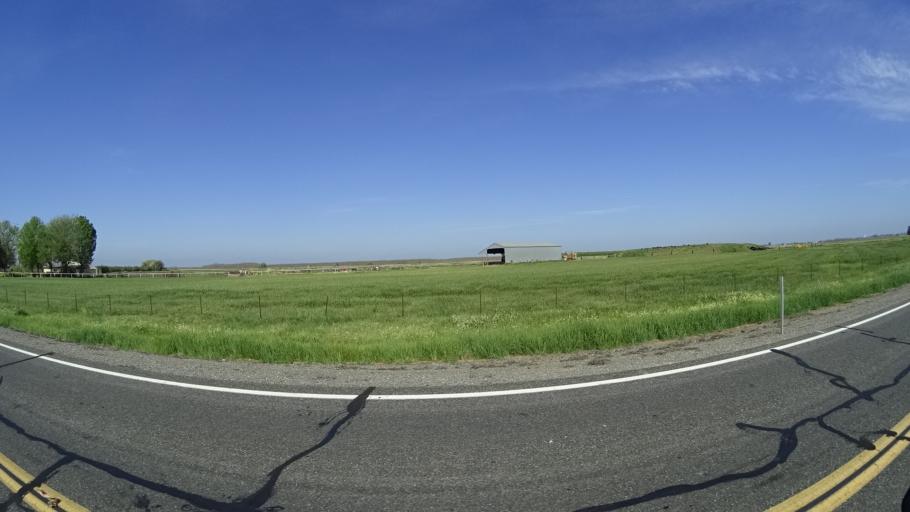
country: US
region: California
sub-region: Glenn County
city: Hamilton City
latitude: 39.6726
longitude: -122.0076
